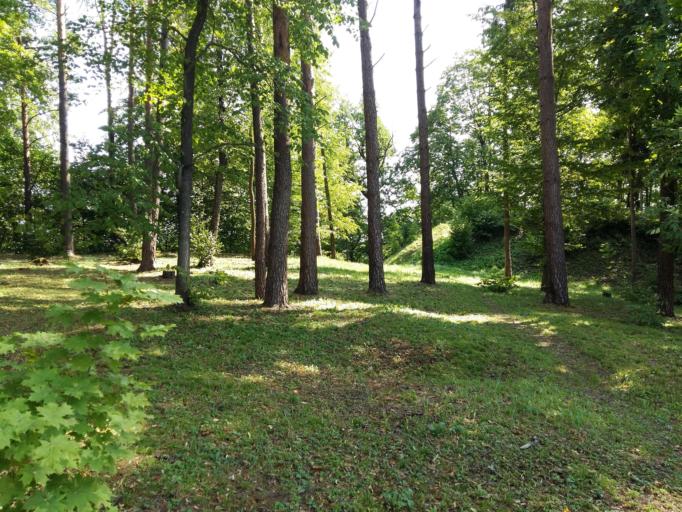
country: LT
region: Kauno apskritis
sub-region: Kauno rajonas
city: Karmelava
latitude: 55.0202
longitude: 24.1065
